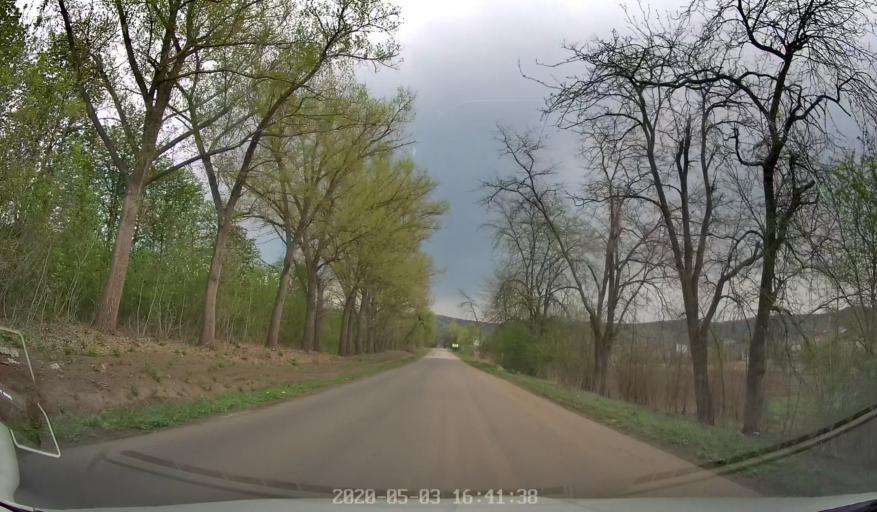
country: MD
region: Stinga Nistrului
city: Bucovat
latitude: 47.1651
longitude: 28.4108
